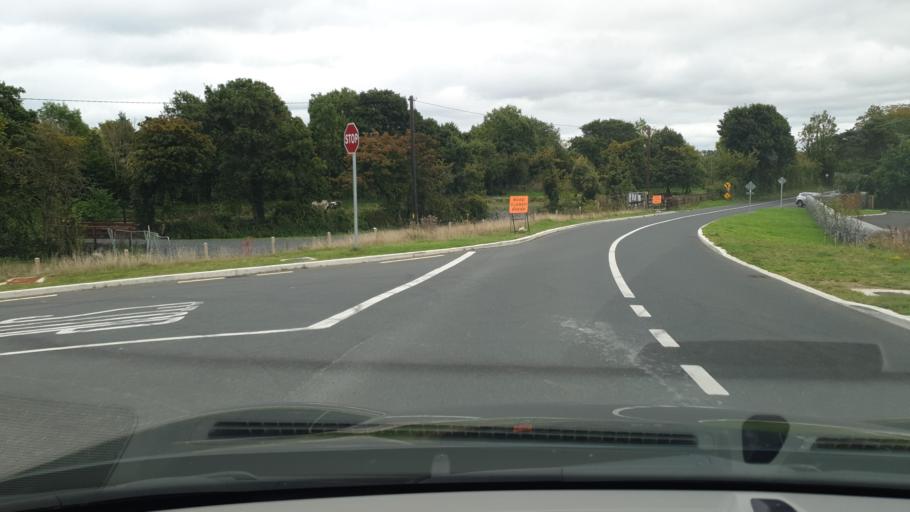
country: IE
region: Leinster
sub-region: Kildare
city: Sallins
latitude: 53.2425
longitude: -6.6753
